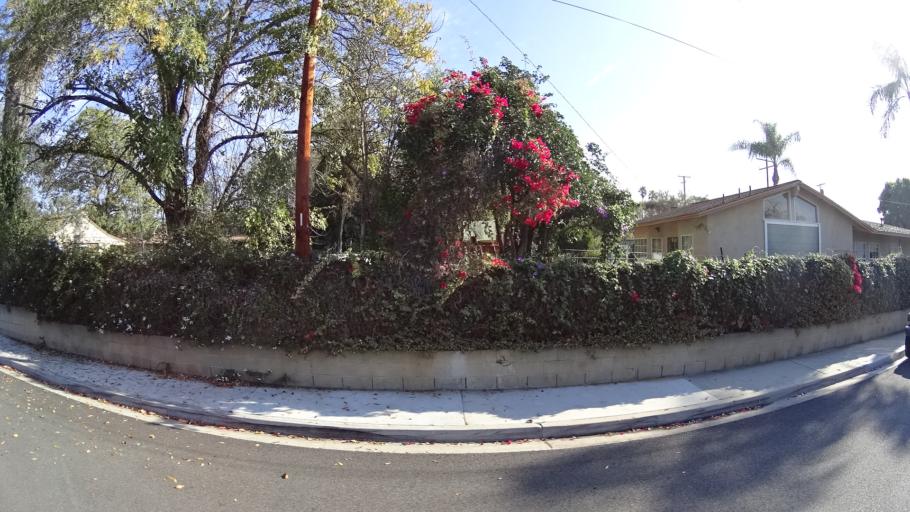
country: US
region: California
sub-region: Orange County
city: Tustin
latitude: 33.7537
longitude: -117.8127
